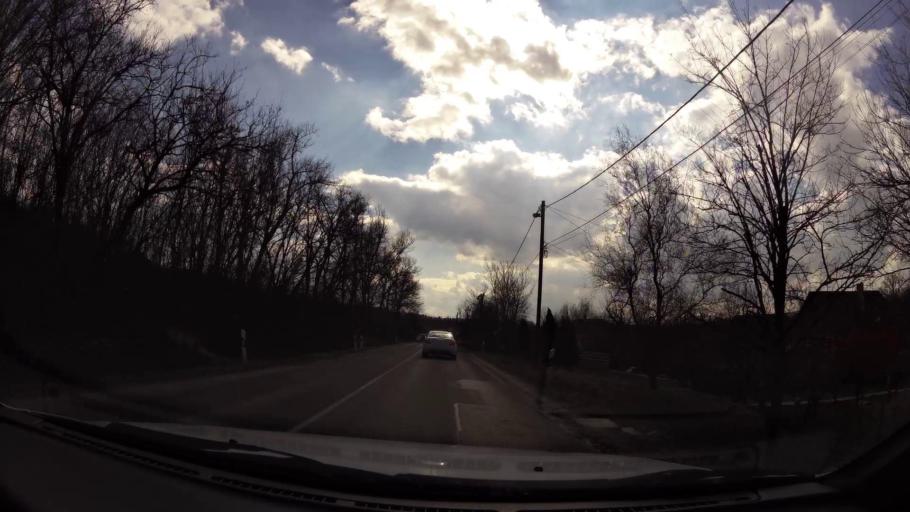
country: HU
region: Pest
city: Mende
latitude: 47.4345
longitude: 19.4632
